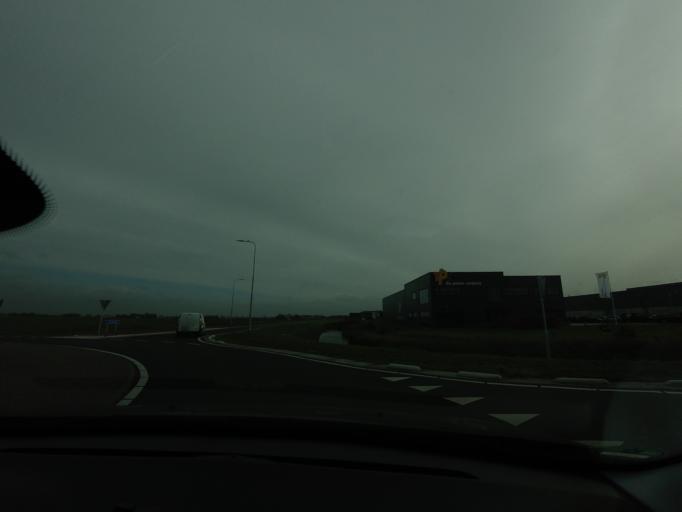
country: NL
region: Flevoland
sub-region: Gemeente Noordoostpolder
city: Emmeloord
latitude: 52.7188
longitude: 5.7844
